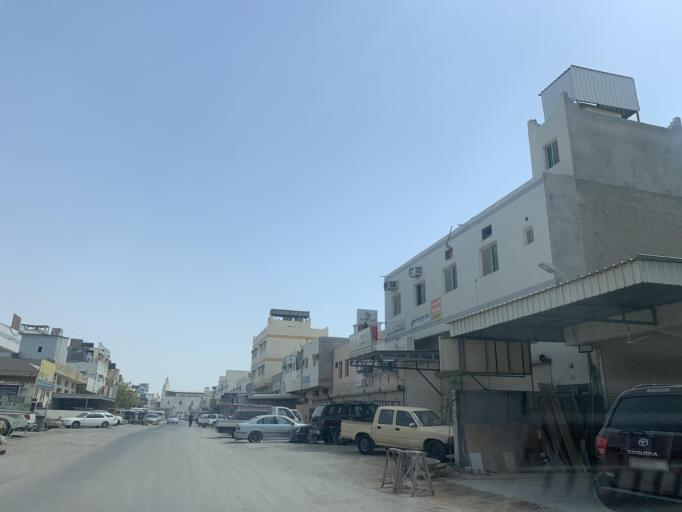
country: BH
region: Central Governorate
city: Madinat Hamad
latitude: 26.1397
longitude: 50.4843
